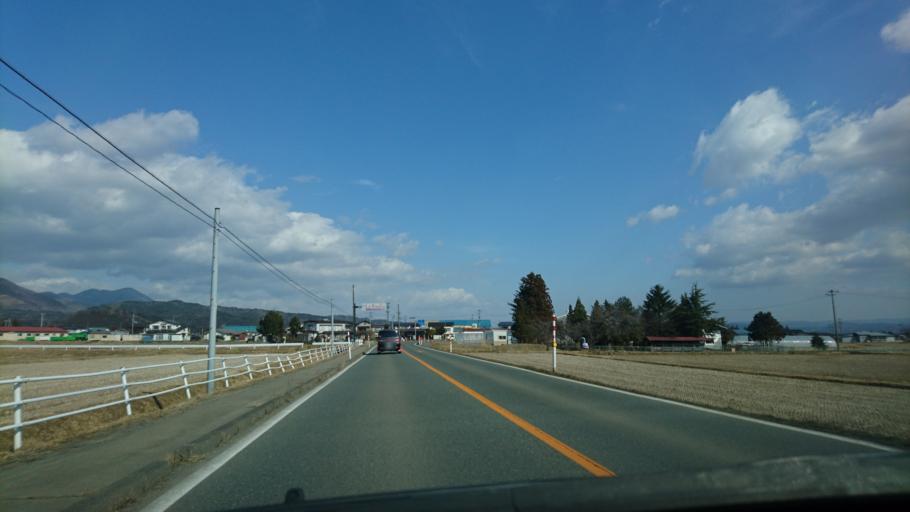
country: JP
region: Iwate
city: Morioka-shi
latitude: 39.5660
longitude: 141.1084
